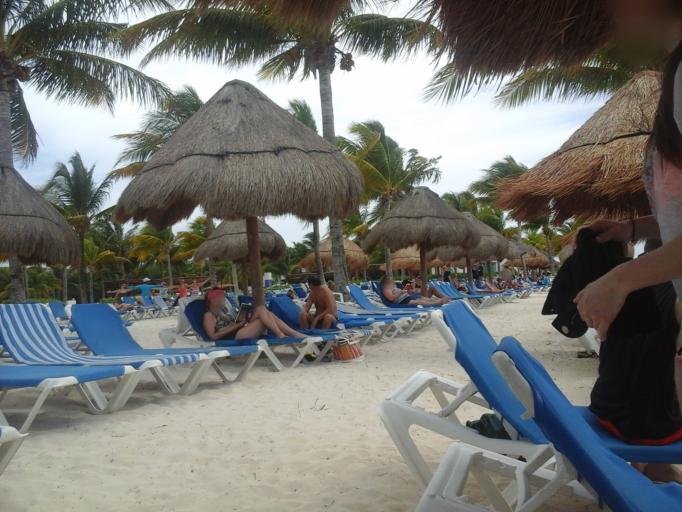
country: MX
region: Quintana Roo
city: Playa del Carmen
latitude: 20.6998
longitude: -87.0124
